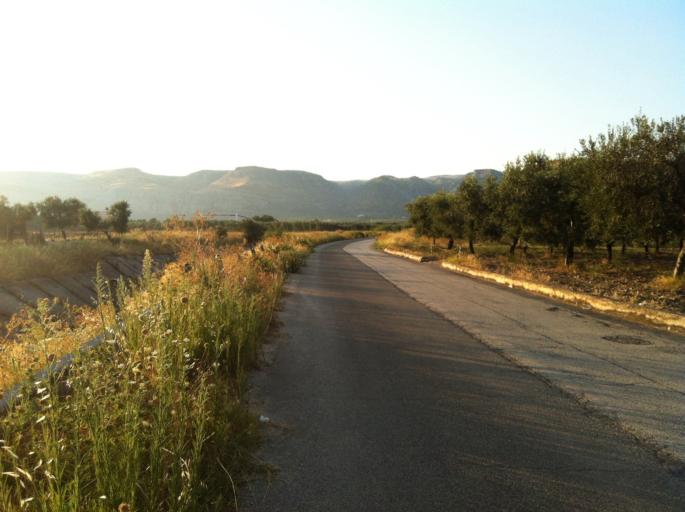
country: IT
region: Apulia
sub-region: Provincia di Foggia
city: Manfredonia
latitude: 41.6495
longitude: 15.9557
